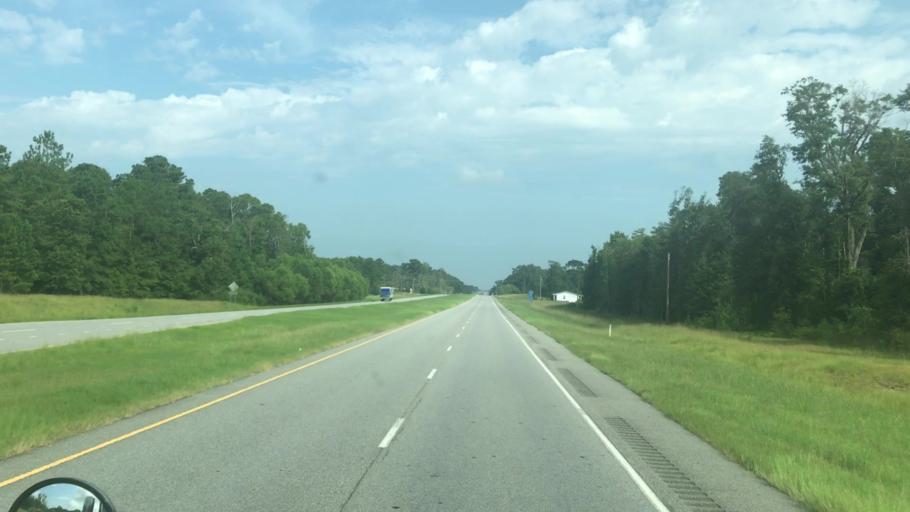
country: US
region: Georgia
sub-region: Early County
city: Blakely
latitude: 31.2899
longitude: -84.8479
